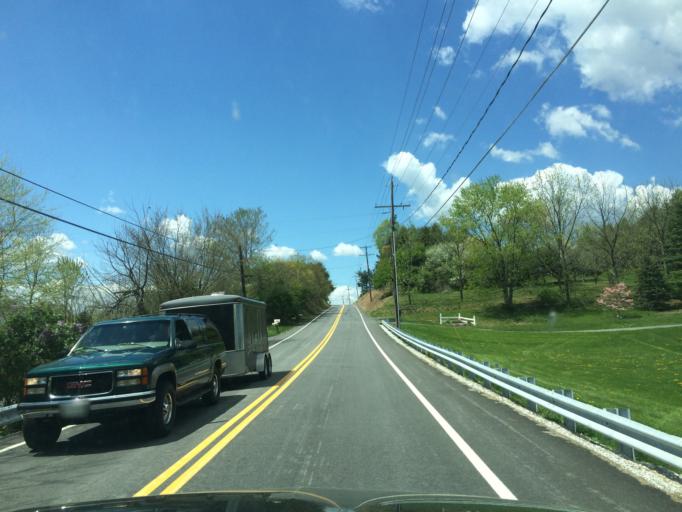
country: US
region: Maryland
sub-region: Carroll County
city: Eldersburg
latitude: 39.4345
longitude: -77.0180
